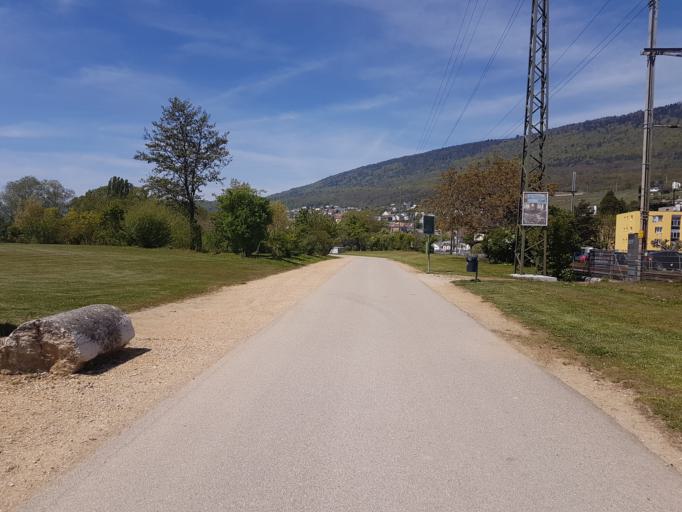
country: CH
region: Neuchatel
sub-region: Neuchatel District
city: Saint-Blaise
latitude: 47.0118
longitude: 6.9864
